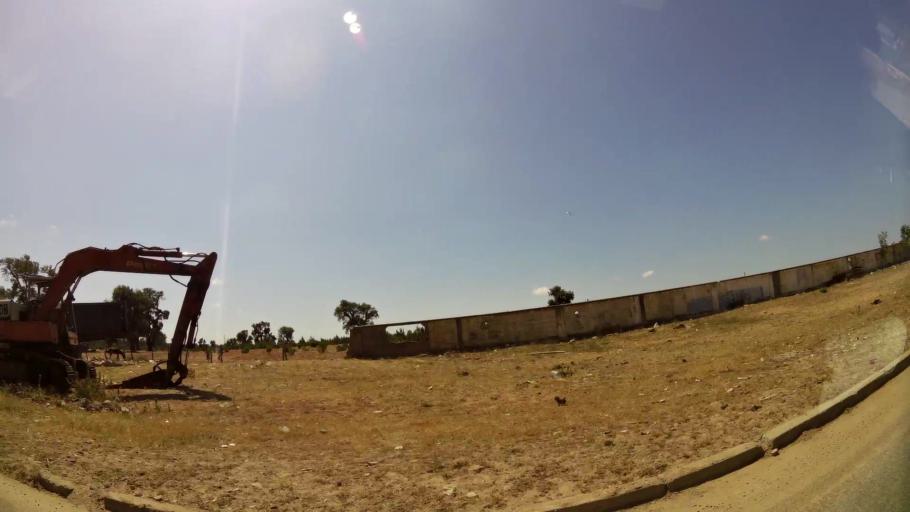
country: MA
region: Gharb-Chrarda-Beni Hssen
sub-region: Kenitra Province
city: Kenitra
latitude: 34.2316
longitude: -6.5522
